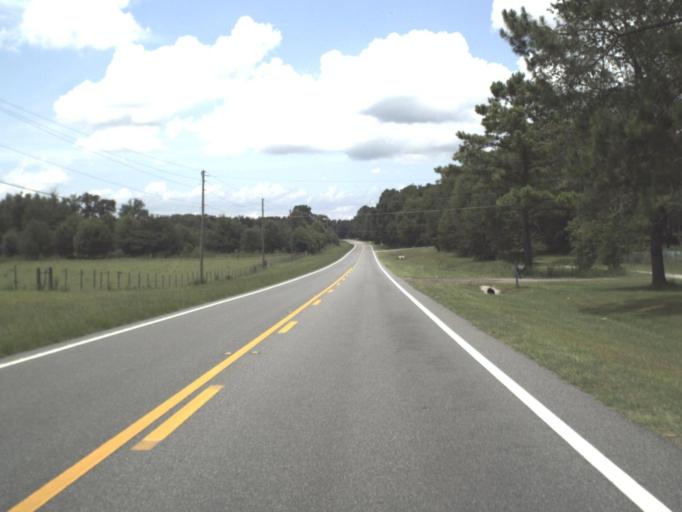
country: US
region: Florida
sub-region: Madison County
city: Madison
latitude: 30.5245
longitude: -83.3682
